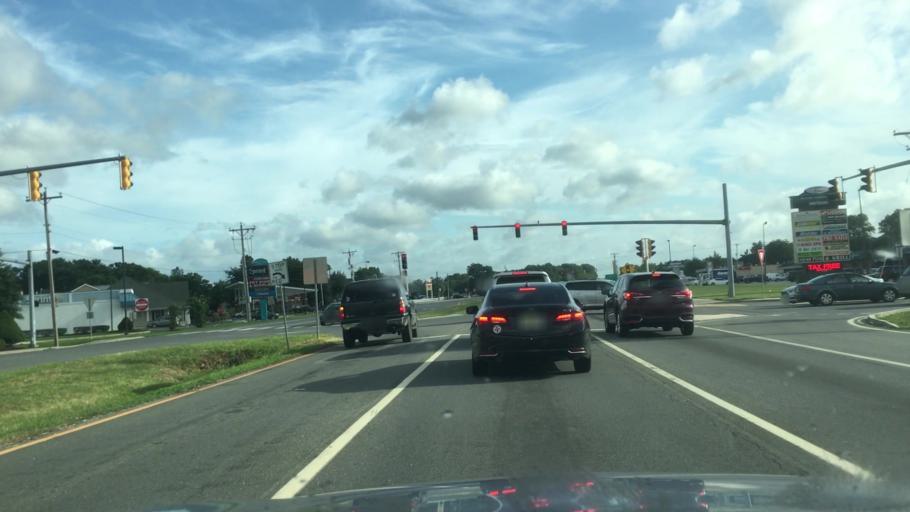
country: US
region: Delaware
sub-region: Sussex County
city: Milford
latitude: 38.9300
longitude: -75.4315
